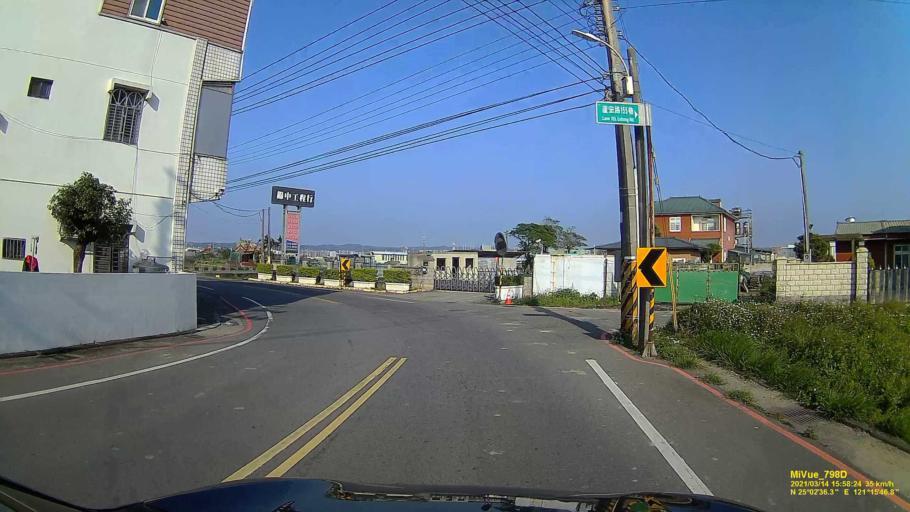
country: TW
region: Taiwan
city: Taoyuan City
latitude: 25.0434
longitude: 121.2631
